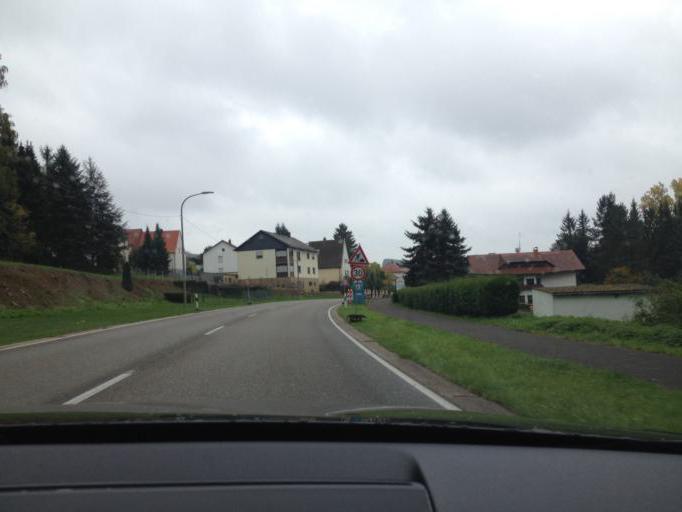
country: DE
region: Rheinland-Pfalz
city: Contwig
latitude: 49.2476
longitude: 7.4512
